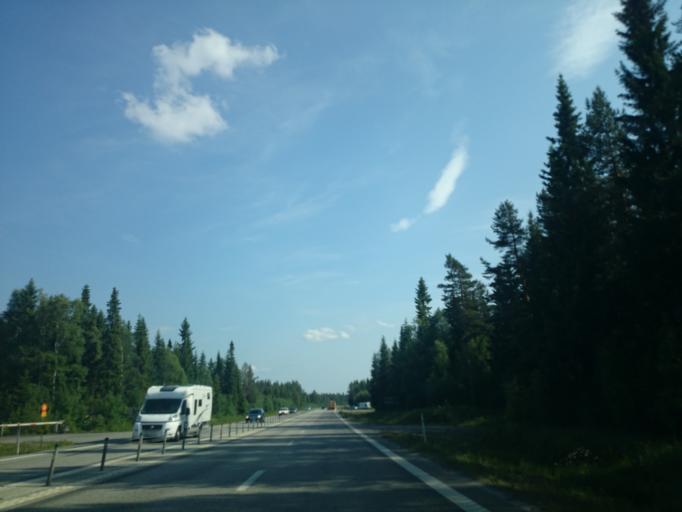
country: SE
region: Jaemtland
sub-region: OEstersunds Kommun
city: Brunflo
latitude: 63.1469
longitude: 14.7785
